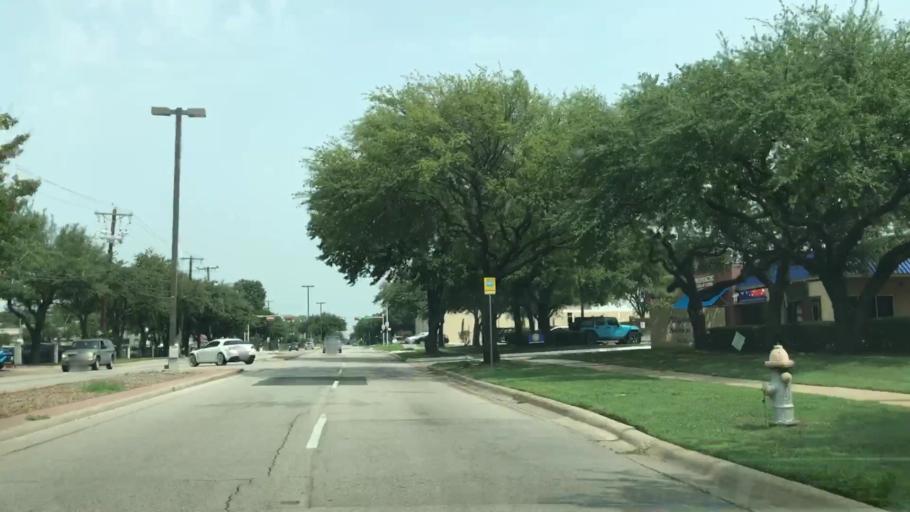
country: US
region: Texas
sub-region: Dallas County
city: Irving
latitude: 32.8522
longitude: -96.9590
